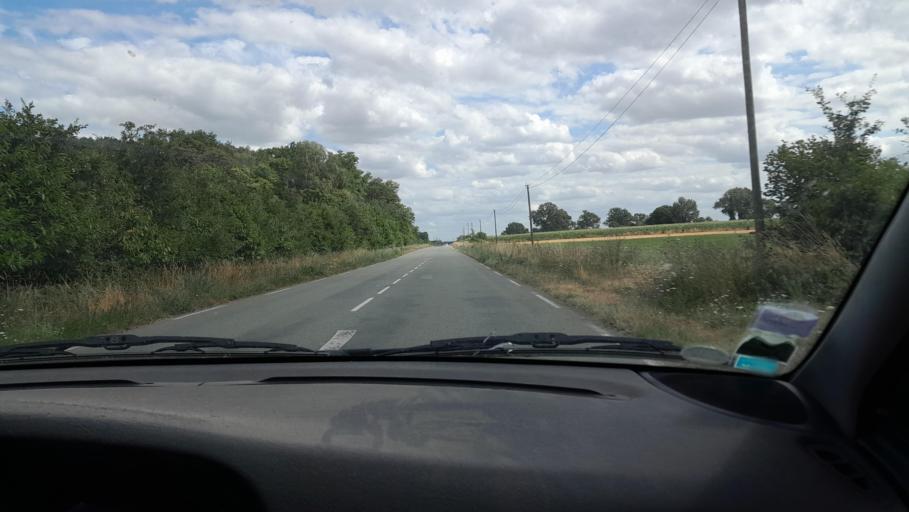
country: FR
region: Pays de la Loire
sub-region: Departement de la Mayenne
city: Ballots
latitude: 47.9402
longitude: -1.0830
